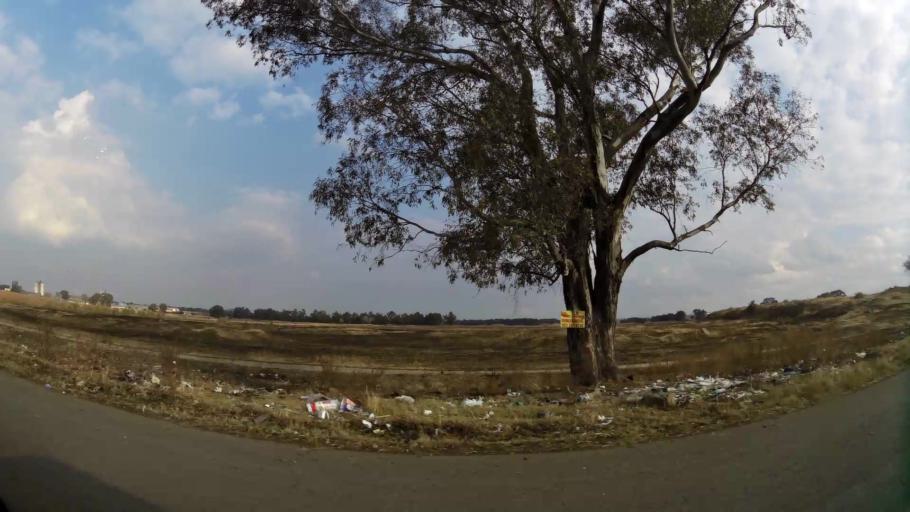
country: ZA
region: Gauteng
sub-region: Sedibeng District Municipality
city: Vereeniging
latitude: -26.6777
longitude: 27.9006
